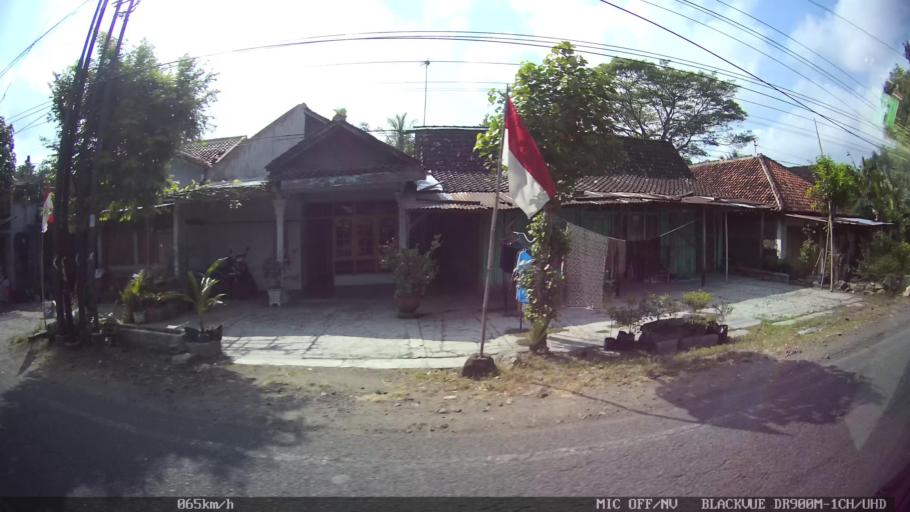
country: ID
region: Daerah Istimewa Yogyakarta
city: Srandakan
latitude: -7.8668
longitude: 110.2103
